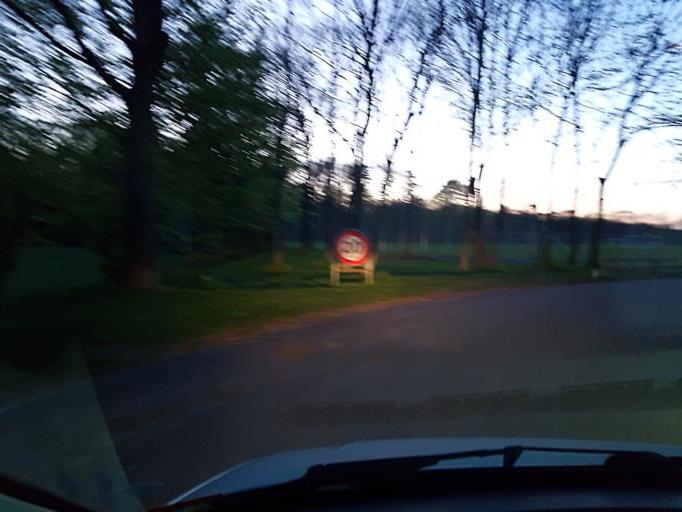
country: DK
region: South Denmark
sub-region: Esbjerg Kommune
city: Esbjerg
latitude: 55.4832
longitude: 8.4358
